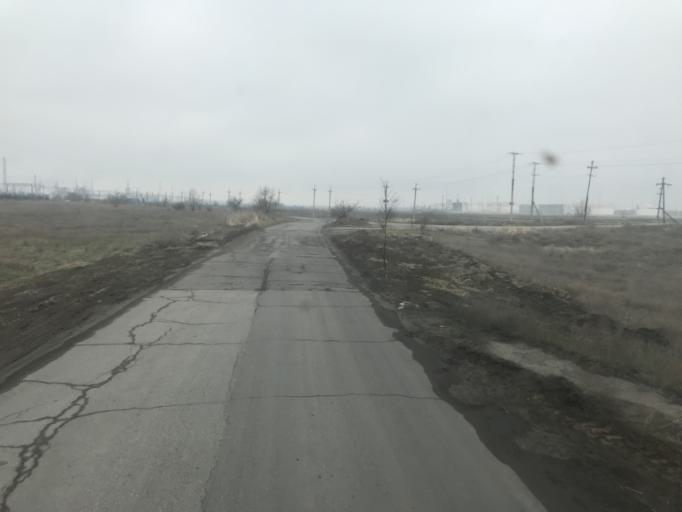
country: RU
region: Volgograd
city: Svetlyy Yar
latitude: 48.4922
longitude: 44.6580
